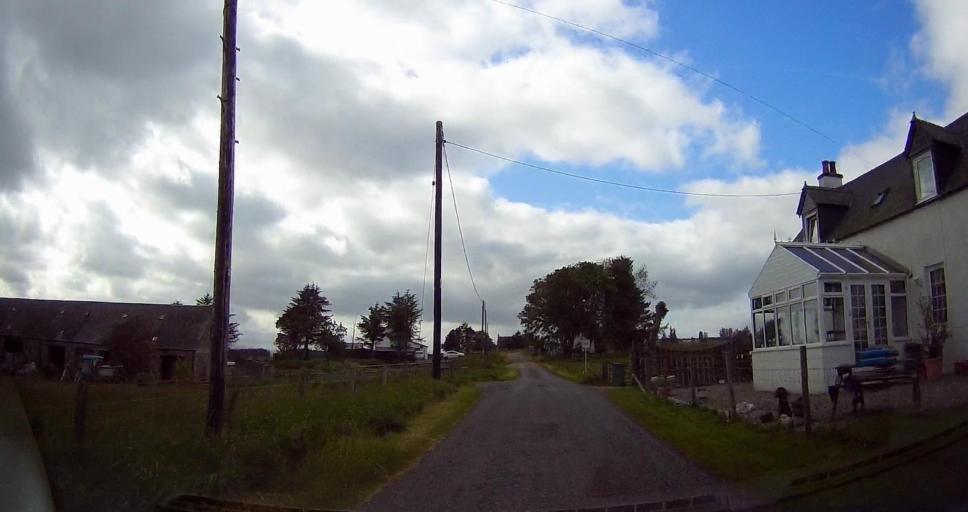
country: GB
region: Scotland
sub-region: Highland
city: Alness
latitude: 58.0714
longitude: -4.4334
